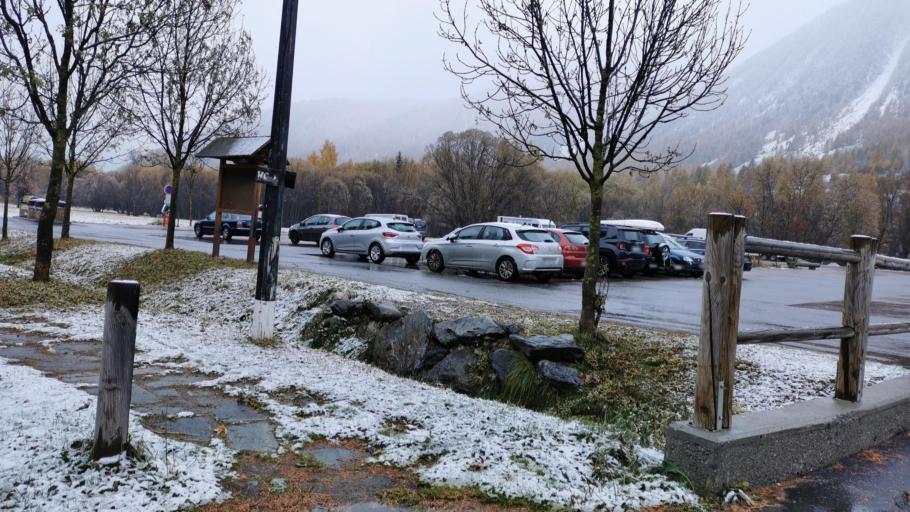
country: FR
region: Provence-Alpes-Cote d'Azur
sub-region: Departement des Hautes-Alpes
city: Villeneuve
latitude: 45.0194
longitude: 6.6070
